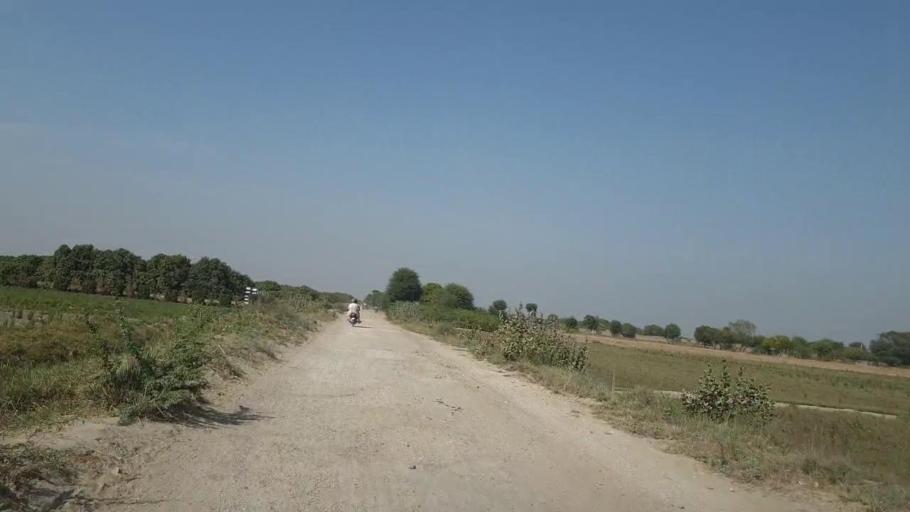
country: PK
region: Sindh
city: Nabisar
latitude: 25.0226
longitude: 69.5244
